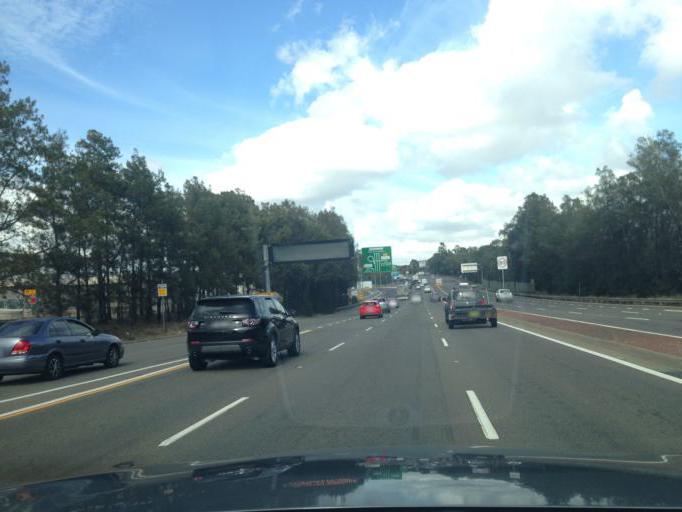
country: AU
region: New South Wales
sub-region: Canada Bay
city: Concord West
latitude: -33.8549
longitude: 151.0753
